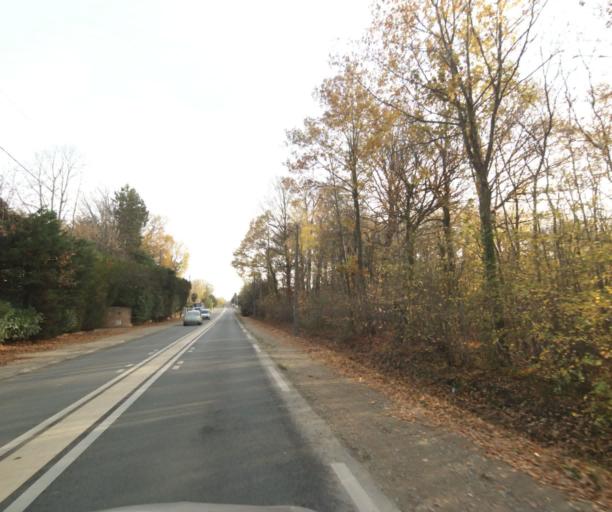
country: FR
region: Ile-de-France
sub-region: Departement des Yvelines
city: Triel-sur-Seine
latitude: 48.9995
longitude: 2.0149
